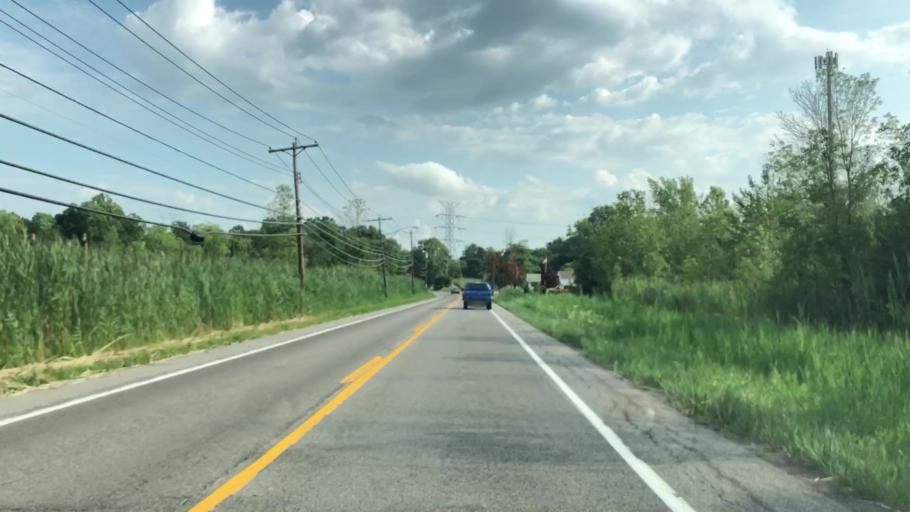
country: US
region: New York
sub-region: Erie County
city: Elma Center
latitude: 42.8326
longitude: -78.6368
